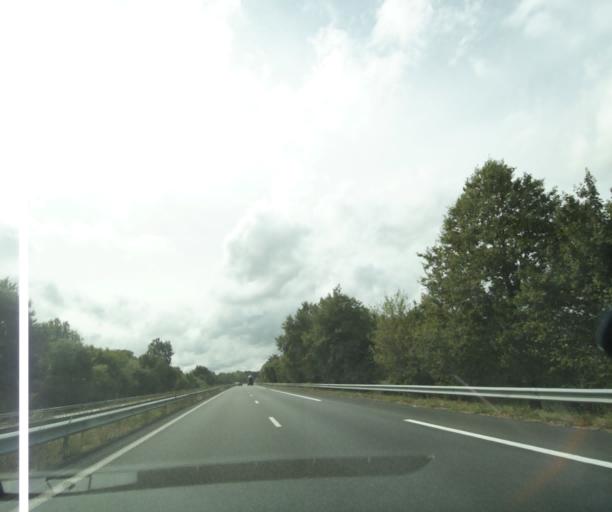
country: FR
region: Poitou-Charentes
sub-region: Departement de la Charente-Maritime
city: Saint-Genis-de-Saintonge
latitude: 45.4987
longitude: -0.6135
